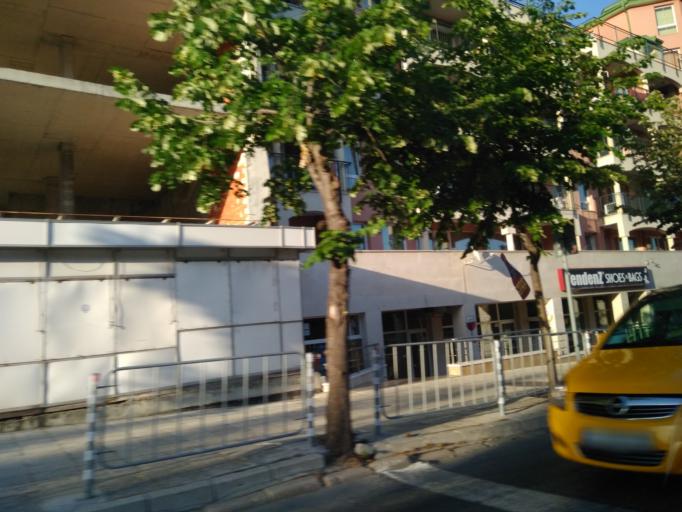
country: BG
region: Burgas
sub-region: Obshtina Nesebur
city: Nesebar
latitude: 42.6611
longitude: 27.7226
